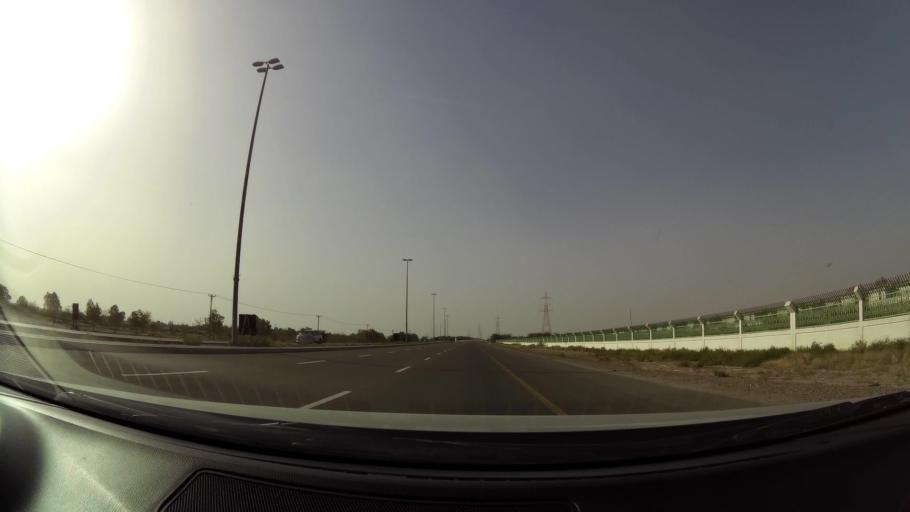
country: AE
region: Abu Dhabi
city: Al Ain
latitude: 24.0836
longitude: 55.7261
